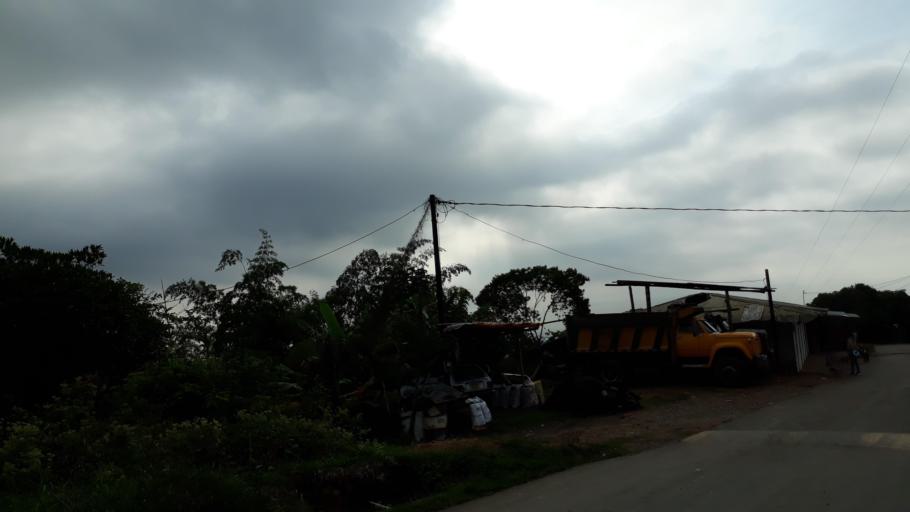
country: CO
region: Valle del Cauca
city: Jamundi
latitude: 3.2072
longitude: -76.6318
